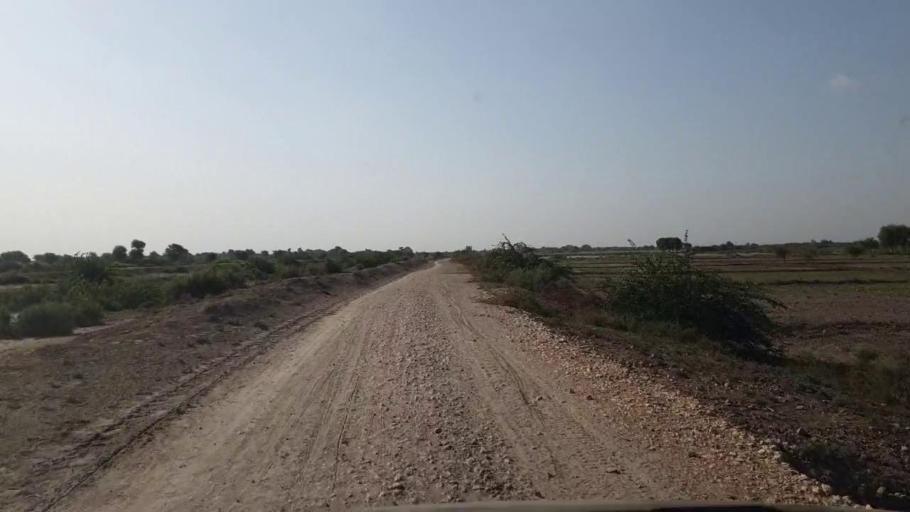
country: PK
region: Sindh
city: Kadhan
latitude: 24.6259
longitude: 69.0733
